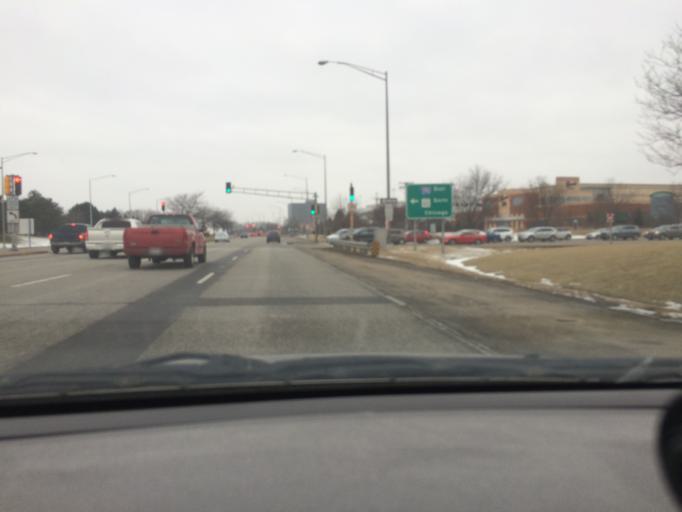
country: US
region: Illinois
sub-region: Cook County
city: Hoffman Estates
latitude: 42.0371
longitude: -88.0317
